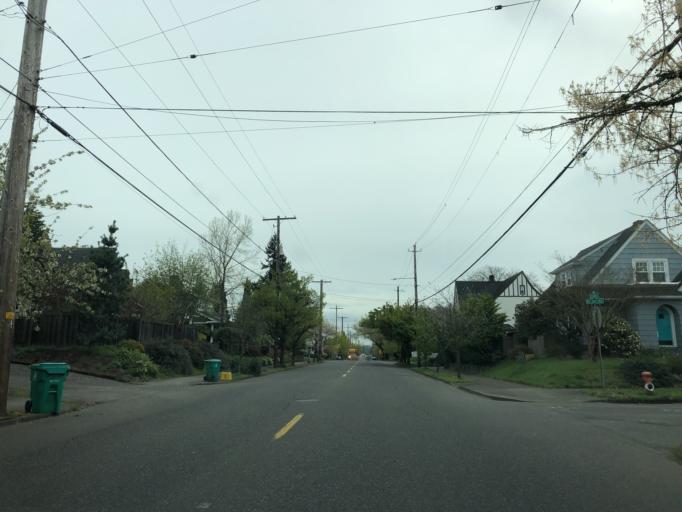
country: US
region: Oregon
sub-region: Multnomah County
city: Portland
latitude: 45.5483
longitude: -122.6274
